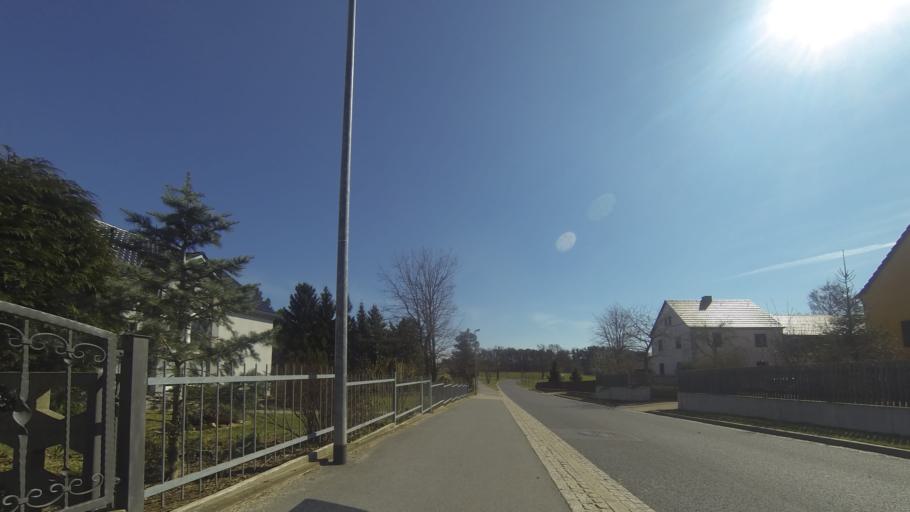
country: DE
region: Saxony
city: Ottendorf-Okrilla
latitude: 51.1752
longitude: 13.7895
